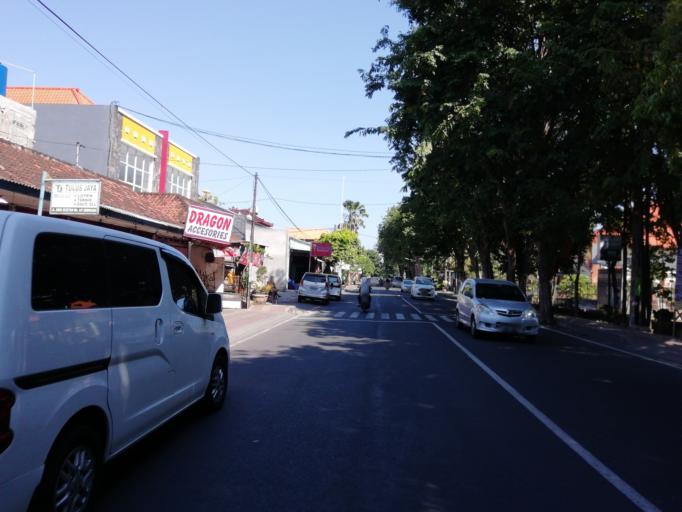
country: ID
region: Bali
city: Karyadharma
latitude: -8.7019
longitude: 115.2196
